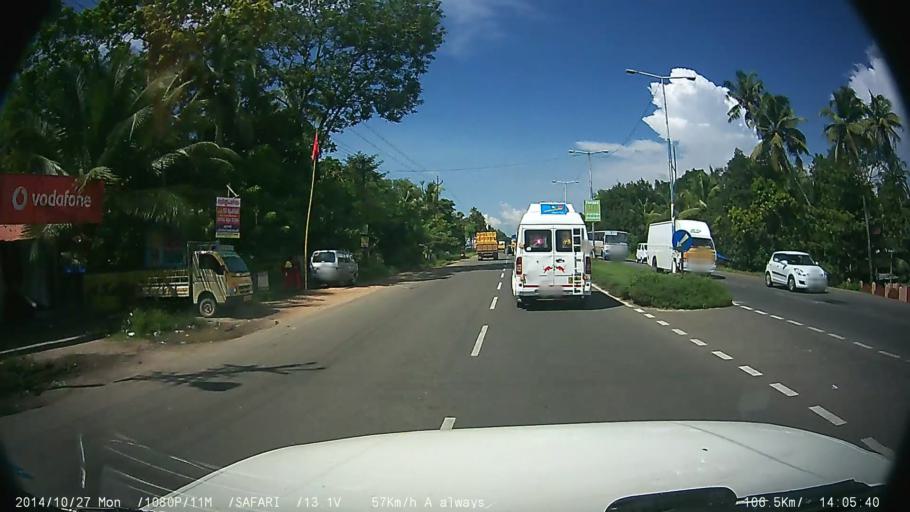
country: IN
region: Kerala
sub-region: Alappuzha
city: Vayalar
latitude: 9.7430
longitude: 76.3186
